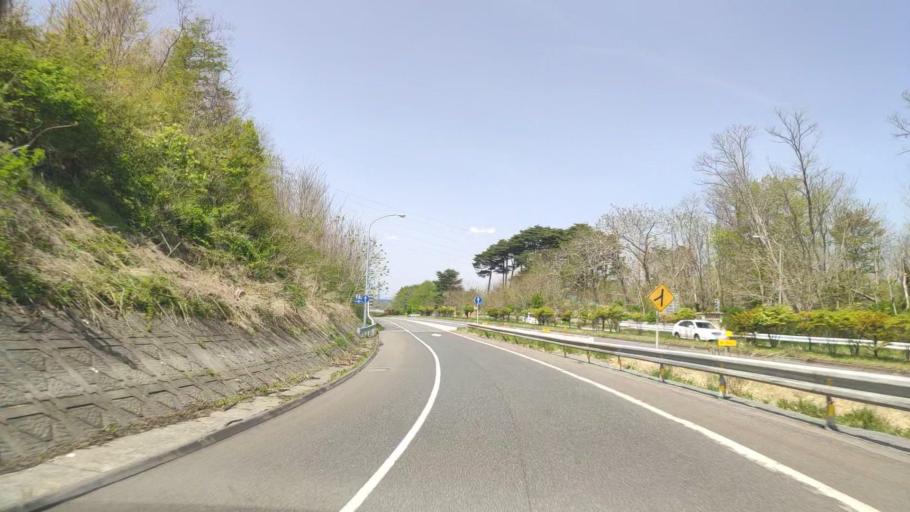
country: JP
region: Aomori
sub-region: Hachinohe Shi
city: Uchimaru
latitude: 40.4946
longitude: 141.4640
